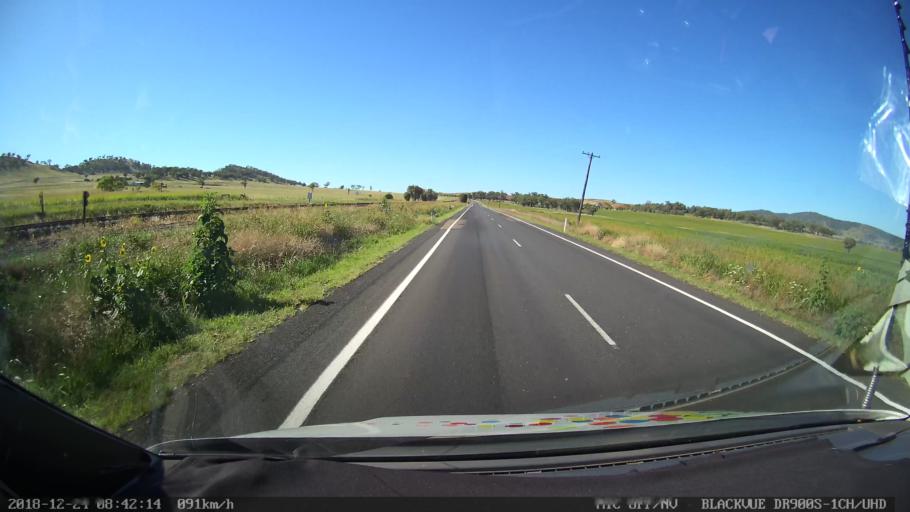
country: AU
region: New South Wales
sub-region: Liverpool Plains
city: Quirindi
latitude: -31.3719
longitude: 150.6433
